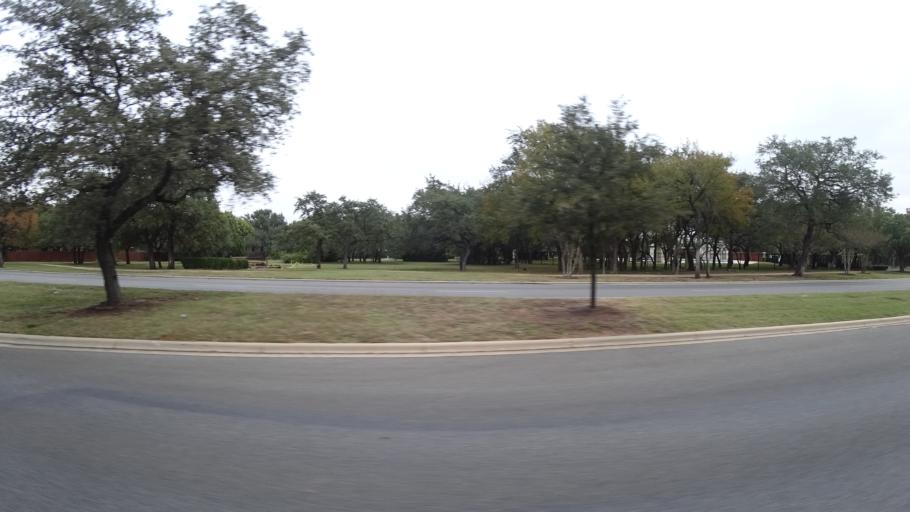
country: US
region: Texas
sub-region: Williamson County
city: Cedar Park
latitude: 30.4853
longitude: -97.8381
